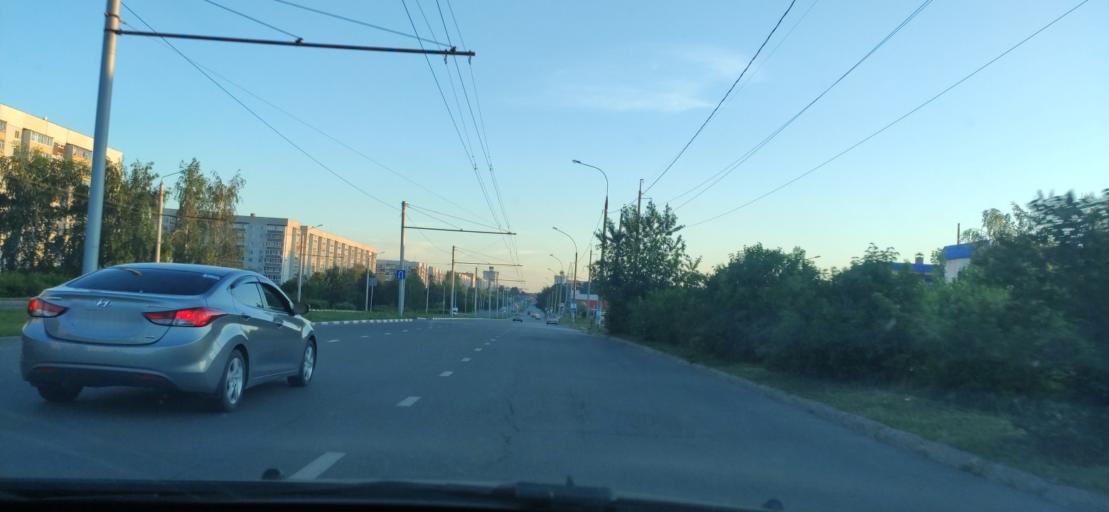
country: RU
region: Ulyanovsk
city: Mirnyy
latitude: 54.3871
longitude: 48.6078
